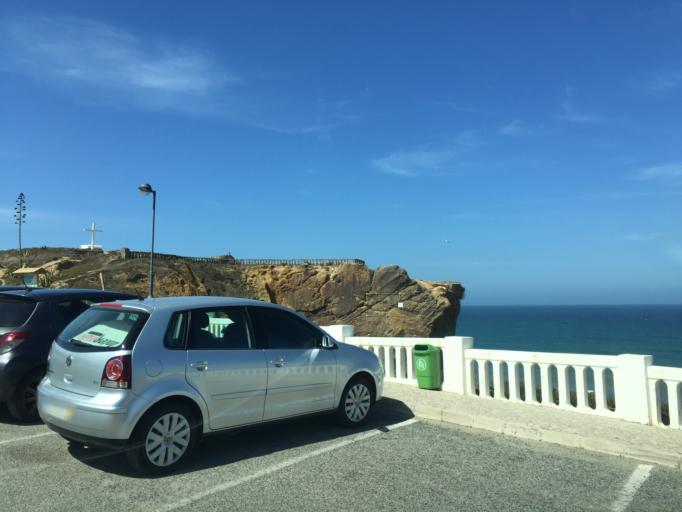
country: PT
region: Lisbon
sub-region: Torres Vedras
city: Silveira
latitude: 39.1311
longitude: -9.3848
